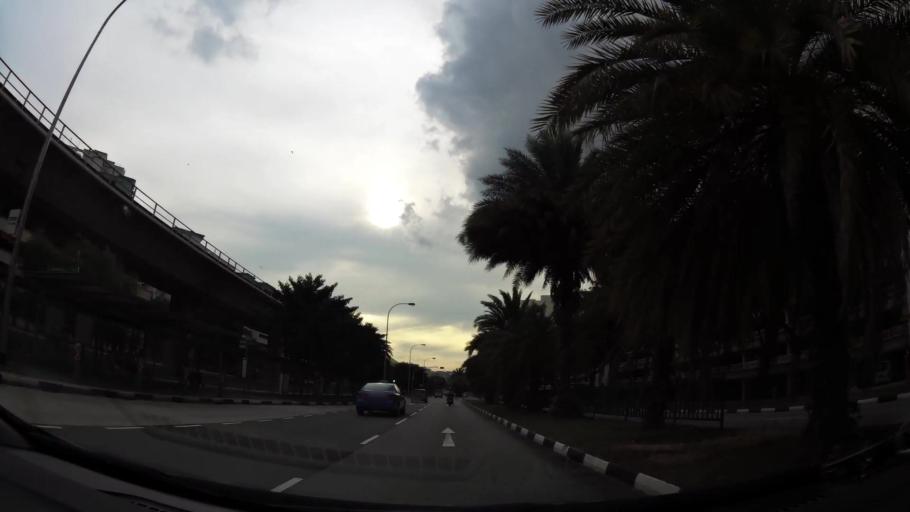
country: MY
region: Johor
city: Johor Bahru
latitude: 1.4487
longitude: 103.8170
